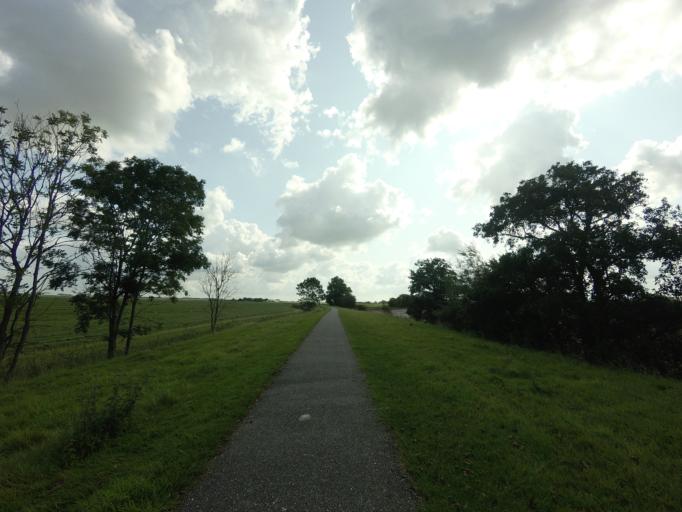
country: NL
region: Friesland
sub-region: Gemeente Het Bildt
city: Minnertsga
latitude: 53.2609
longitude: 5.5919
